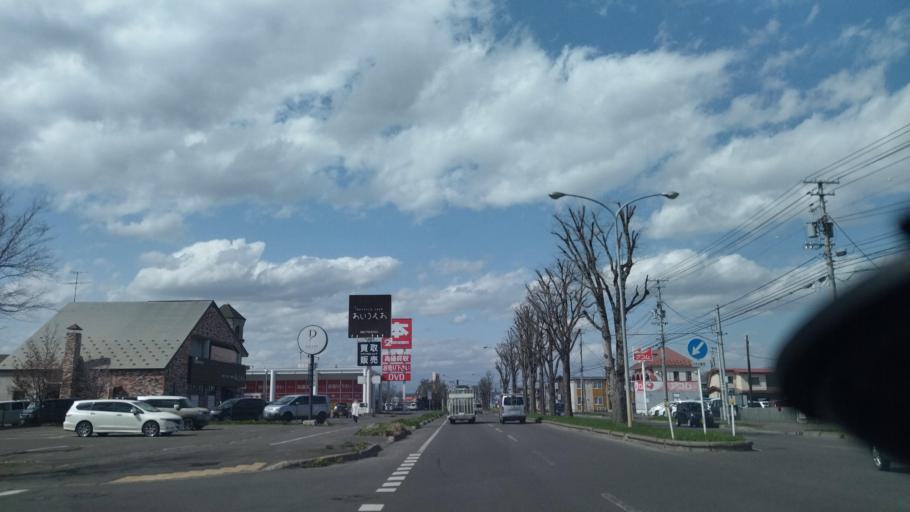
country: JP
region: Hokkaido
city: Obihiro
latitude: 42.9091
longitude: 143.1456
